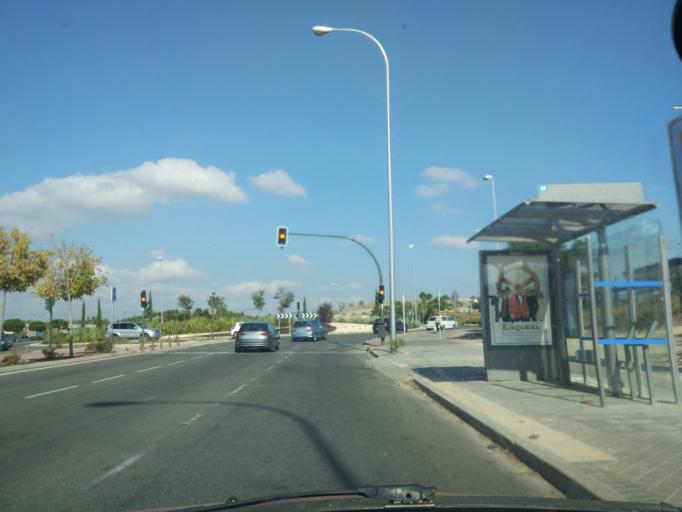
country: ES
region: Madrid
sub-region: Provincia de Madrid
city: Fuencarral-El Pardo
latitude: 40.4952
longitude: -3.7199
